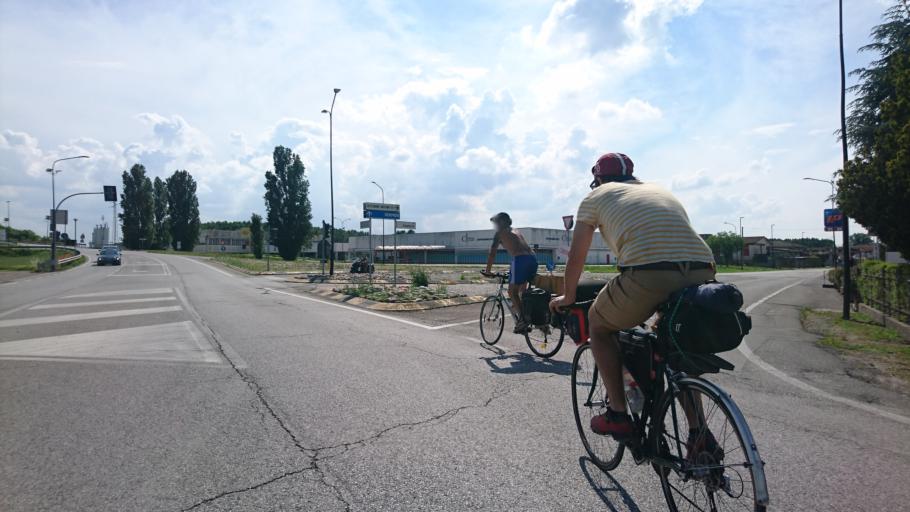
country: IT
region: Veneto
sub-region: Provincia di Rovigo
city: Castelnovo Bariano
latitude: 45.0249
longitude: 11.2946
